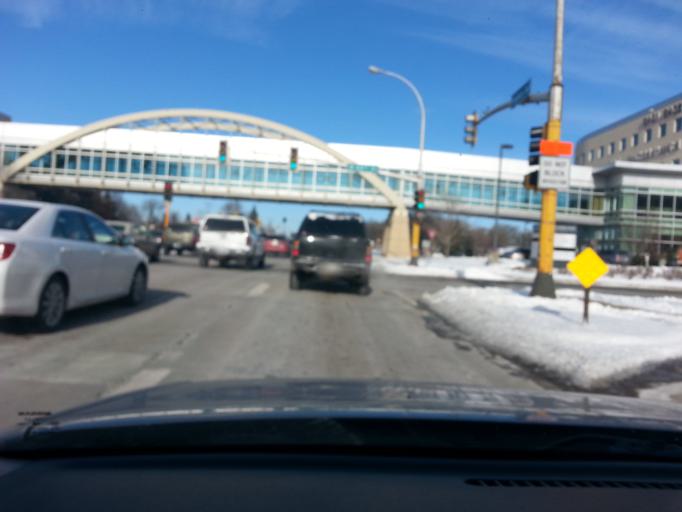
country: US
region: Minnesota
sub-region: Hennepin County
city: Edina
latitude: 44.8854
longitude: -93.3288
